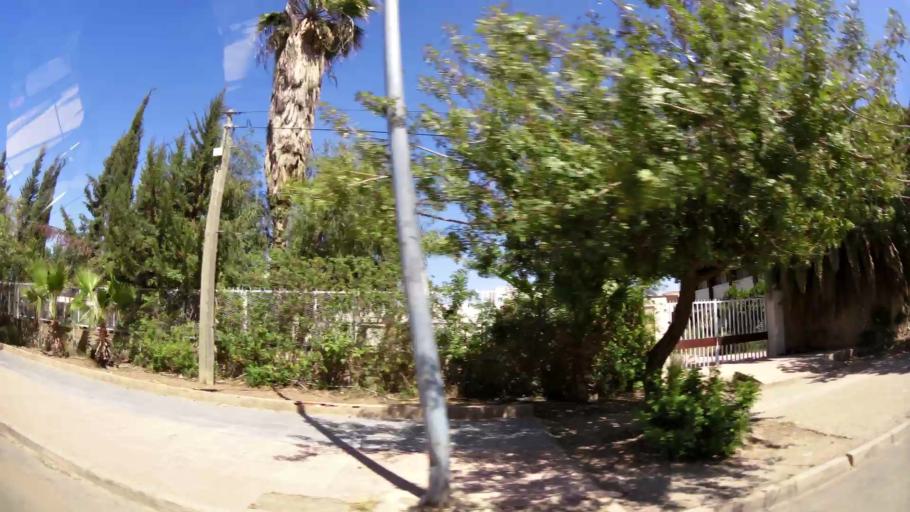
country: MA
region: Oriental
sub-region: Oujda-Angad
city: Oujda
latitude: 34.6529
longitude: -1.9008
